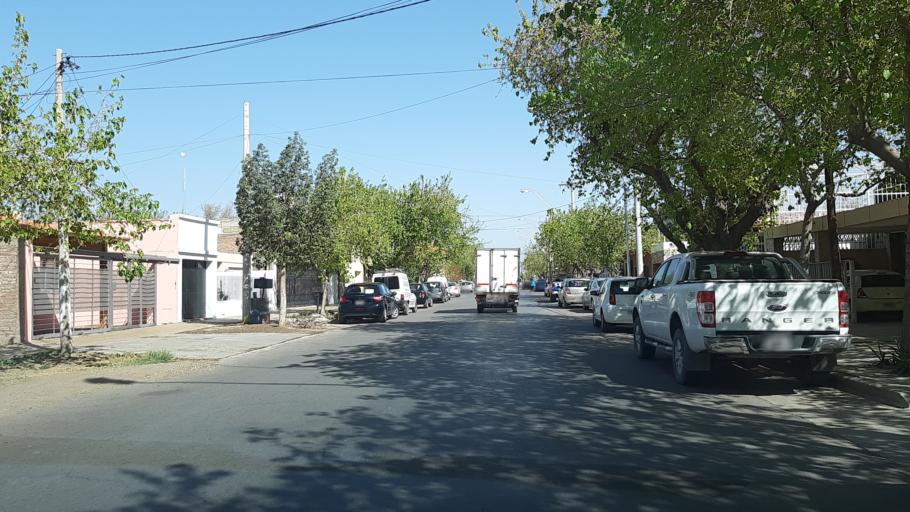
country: AR
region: San Juan
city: San Juan
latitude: -31.5299
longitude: -68.5170
